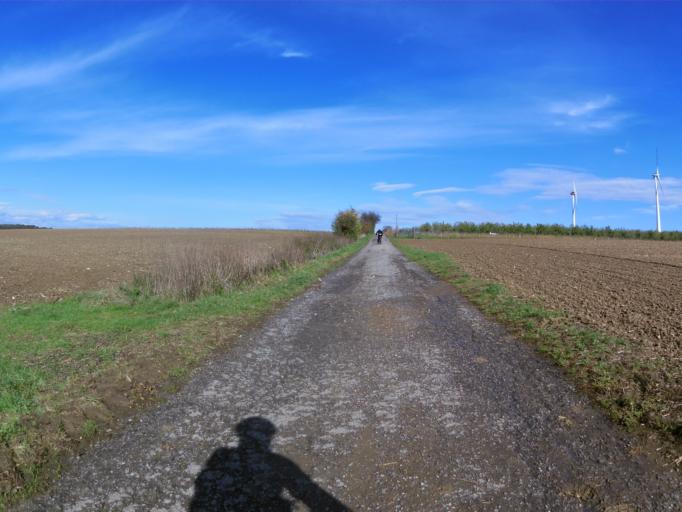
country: DE
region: Bavaria
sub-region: Regierungsbezirk Unterfranken
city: Sommerhausen
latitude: 49.7118
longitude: 10.0392
